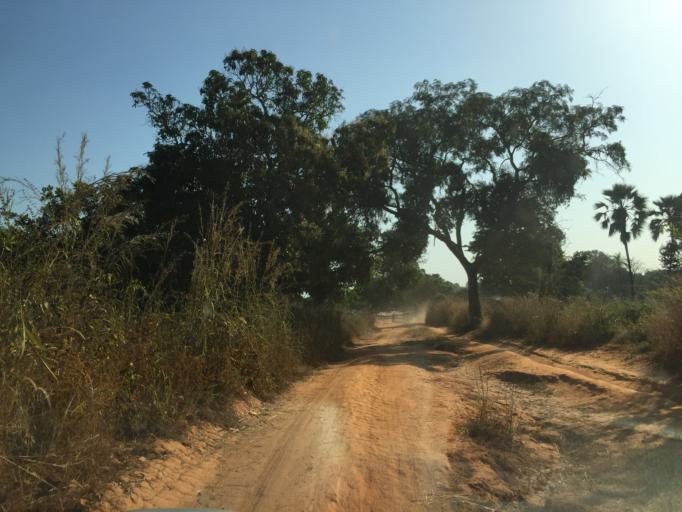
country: GW
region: Oio
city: Farim
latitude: 12.4537
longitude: -15.3078
